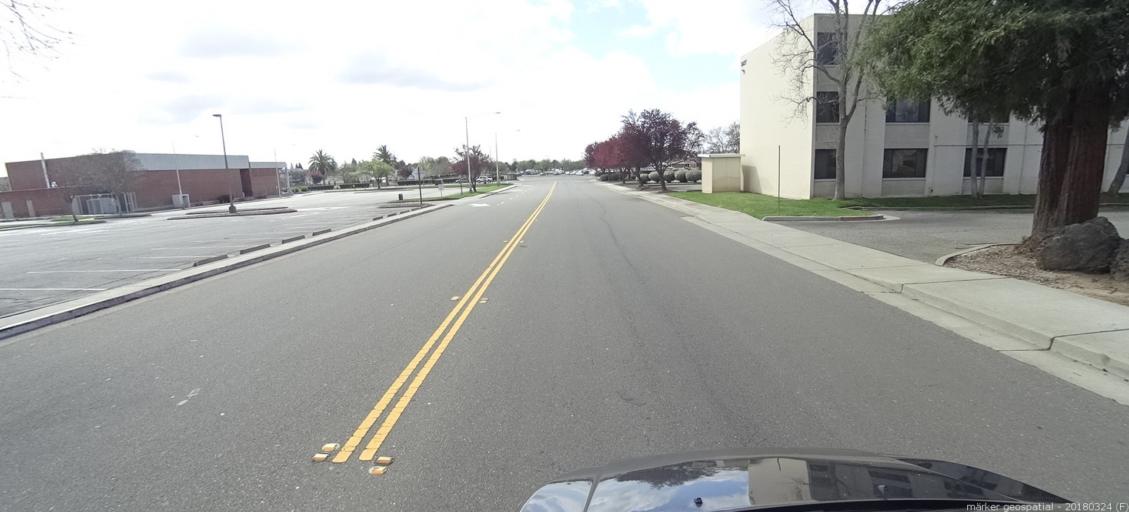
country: US
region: California
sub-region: Sacramento County
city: North Highlands
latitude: 38.6699
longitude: -121.3876
